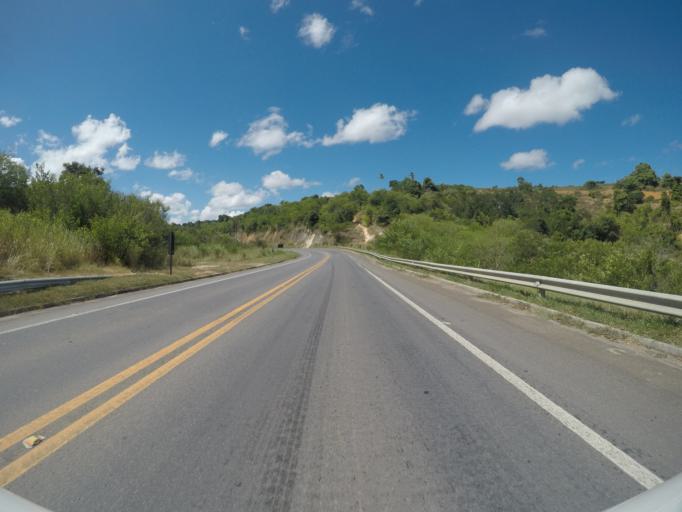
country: BR
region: Espirito Santo
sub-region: Conceicao Da Barra
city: Conceicao da Barra
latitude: -18.2837
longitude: -39.9567
